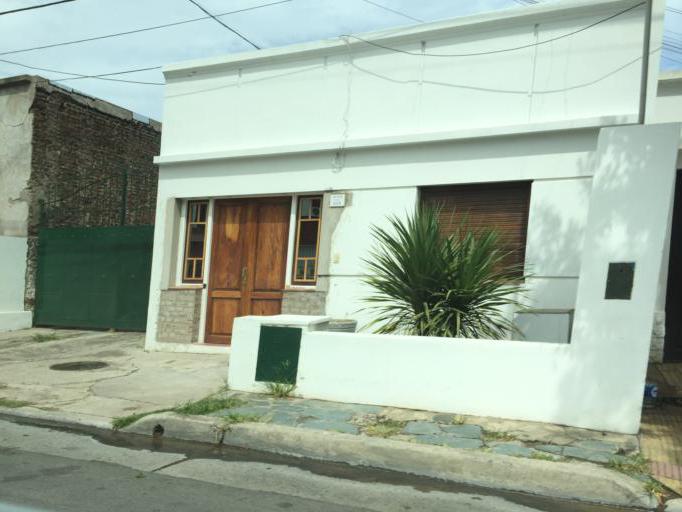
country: AR
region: Buenos Aires
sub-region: Partido de Tandil
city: Tandil
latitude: -37.3265
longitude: -59.1138
